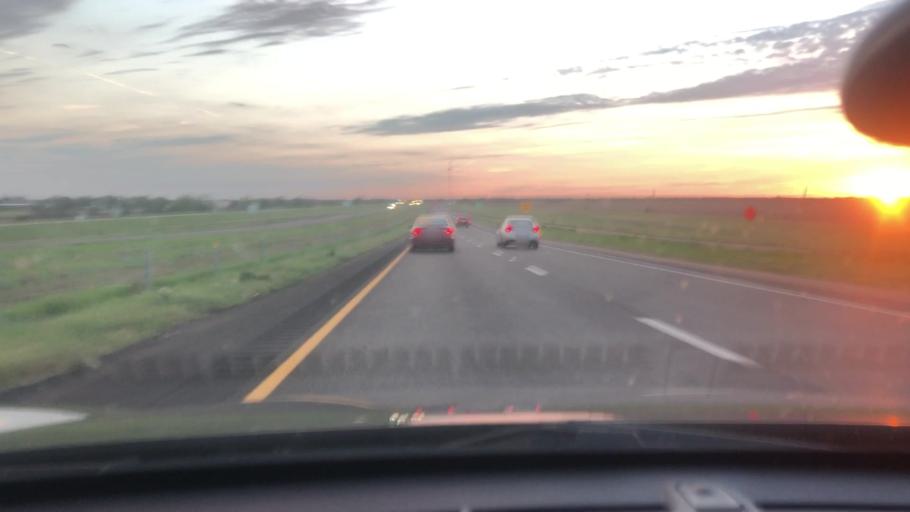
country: US
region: Texas
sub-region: Victoria County
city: Inez
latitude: 28.9332
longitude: -96.7370
